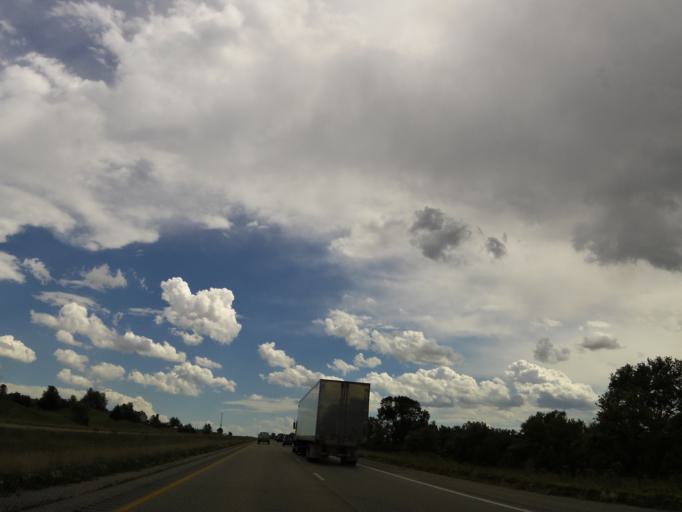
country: US
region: Iowa
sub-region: Johnson County
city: Lone Tree
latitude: 41.4530
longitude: -91.5503
